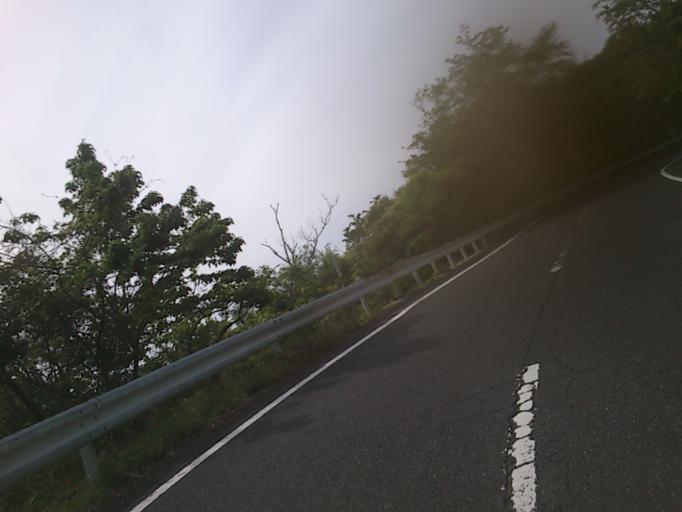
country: JP
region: Hyogo
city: Toyooka
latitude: 35.6880
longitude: 134.9873
